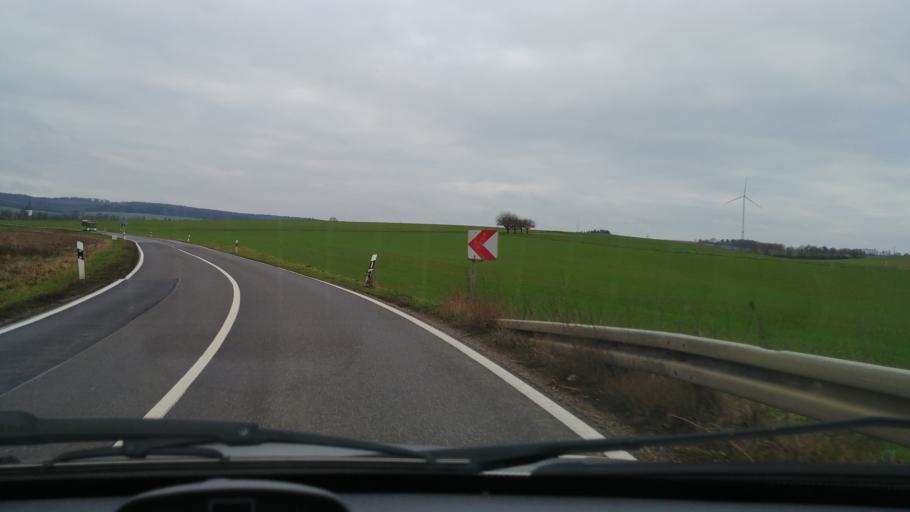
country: DE
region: Rheinland-Pfalz
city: Netzbach
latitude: 50.3214
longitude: 8.1661
